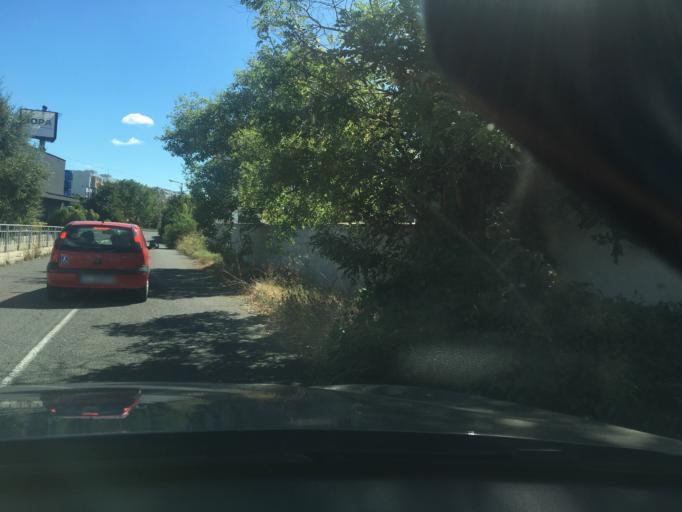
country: BG
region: Burgas
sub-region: Obshtina Burgas
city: Burgas
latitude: 42.5303
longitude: 27.4555
